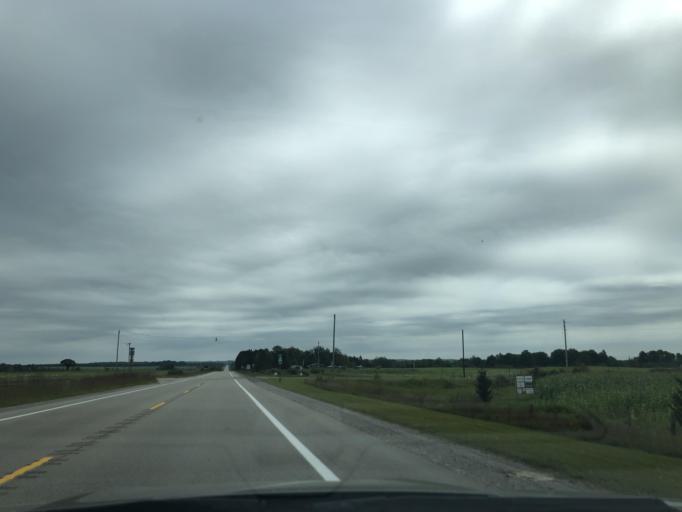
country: US
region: Michigan
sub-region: Clare County
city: Harrison
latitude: 44.0311
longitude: -84.9510
